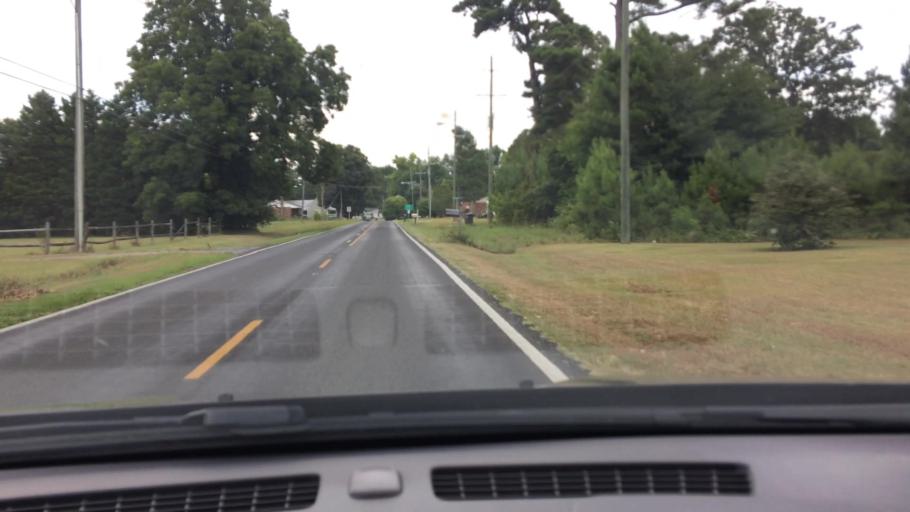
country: US
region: North Carolina
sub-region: Pitt County
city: Ayden
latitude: 35.4607
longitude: -77.4152
